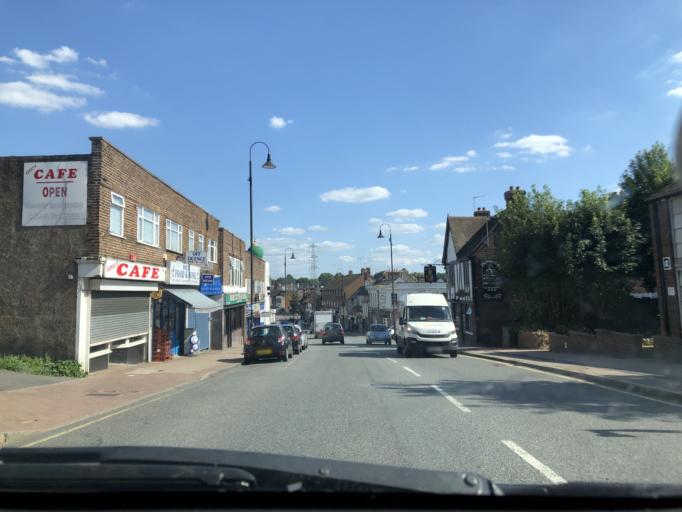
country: GB
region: England
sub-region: Greater London
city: Erith
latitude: 51.4535
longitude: 0.1764
